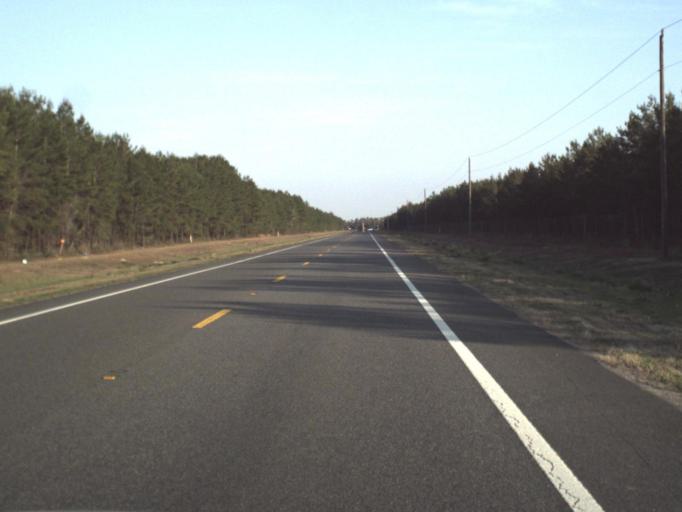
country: US
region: Florida
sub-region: Bay County
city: Lynn Haven
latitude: 30.4369
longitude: -85.6993
